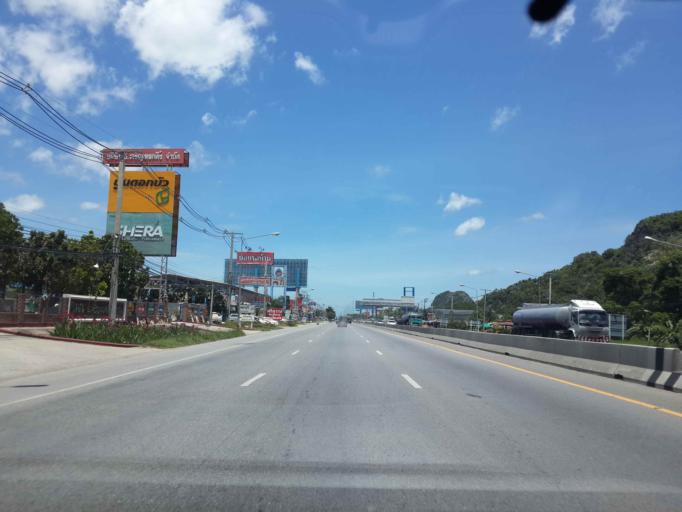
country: TH
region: Phetchaburi
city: Cha-am
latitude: 12.8128
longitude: 99.9425
